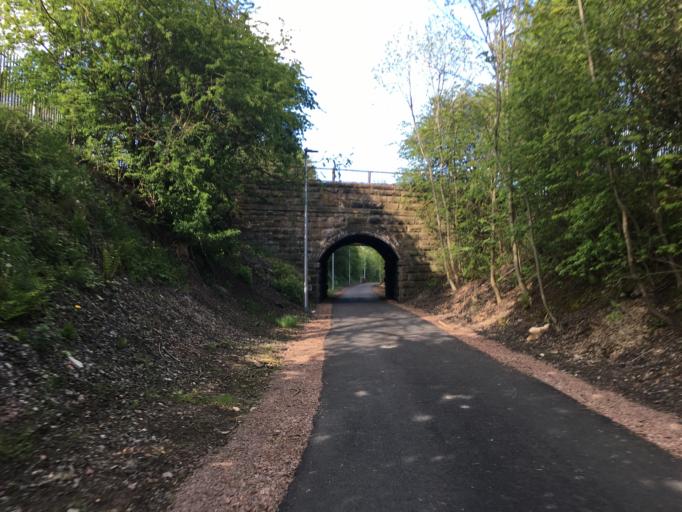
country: GB
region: Scotland
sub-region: Midlothian
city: Bonnyrigg
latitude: 55.9022
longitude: -3.1230
